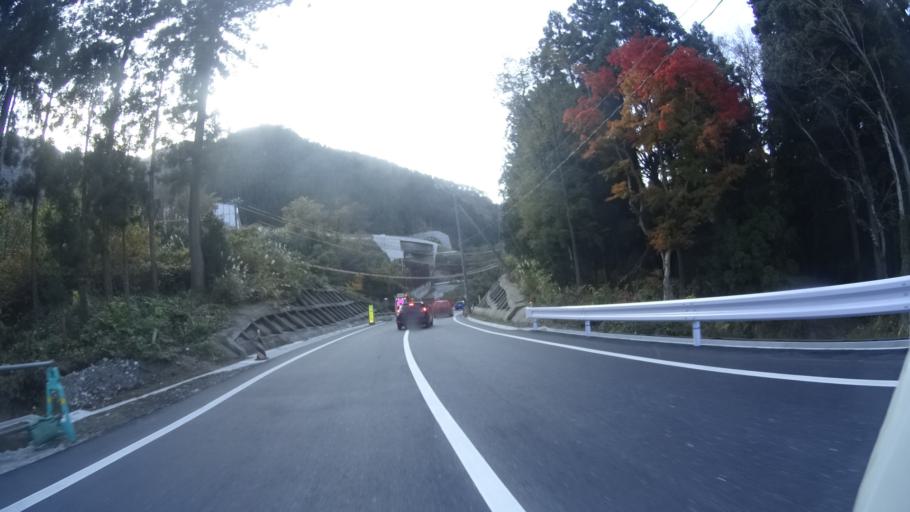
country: JP
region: Fukui
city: Ono
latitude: 35.9650
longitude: 136.6014
